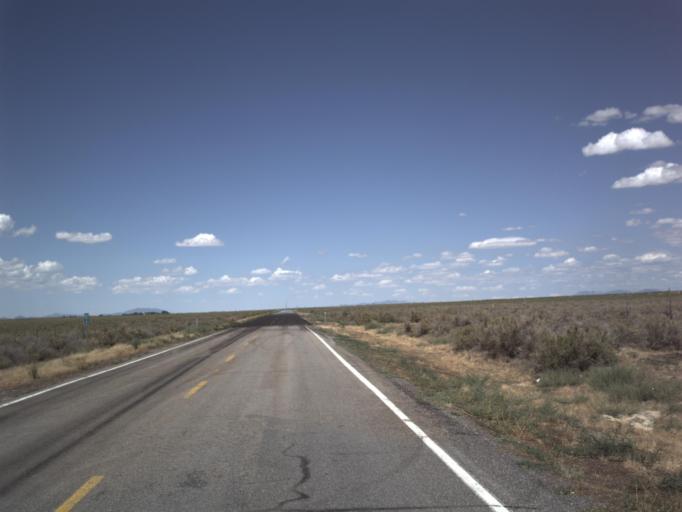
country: US
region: Utah
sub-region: Millard County
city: Delta
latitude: 39.3372
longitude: -112.4904
